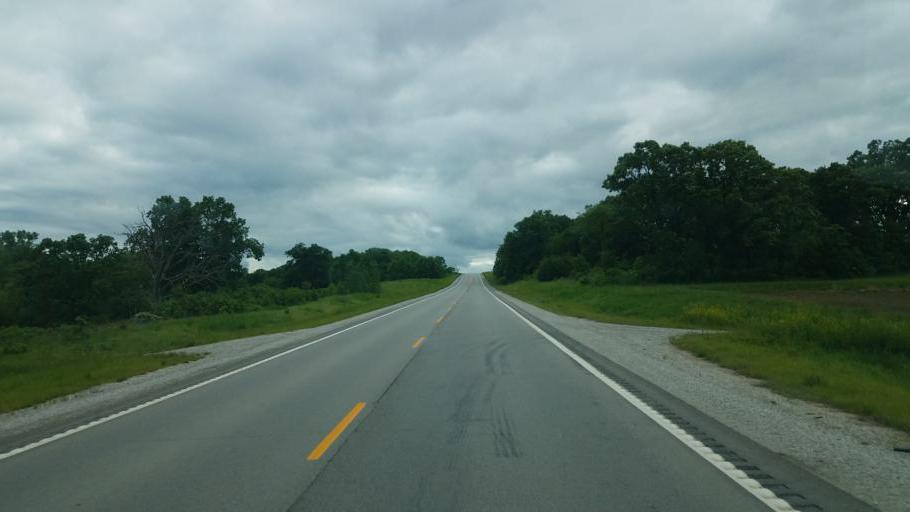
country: US
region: Missouri
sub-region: Harrison County
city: Bethany
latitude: 40.3116
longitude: -93.8100
